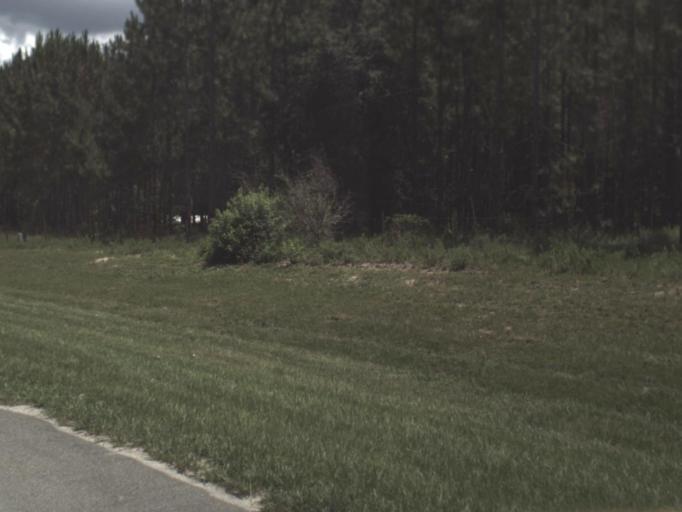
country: US
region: Florida
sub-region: Putnam County
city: Crescent City
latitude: 29.4109
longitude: -81.5097
